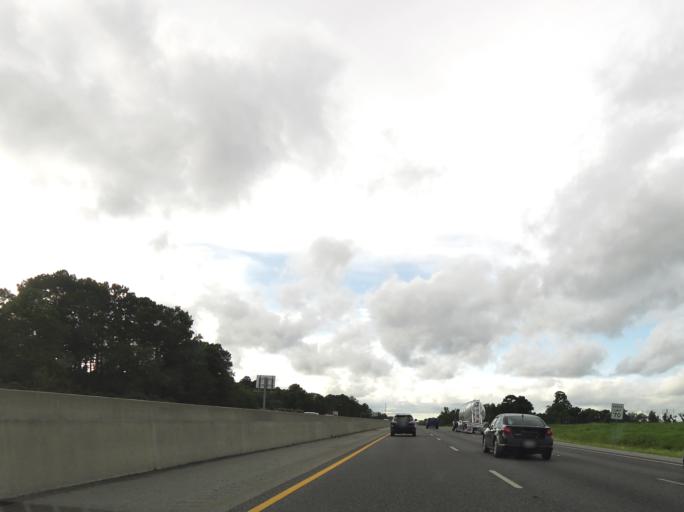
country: US
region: Georgia
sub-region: Turner County
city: Ashburn
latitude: 31.6345
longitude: -83.5828
